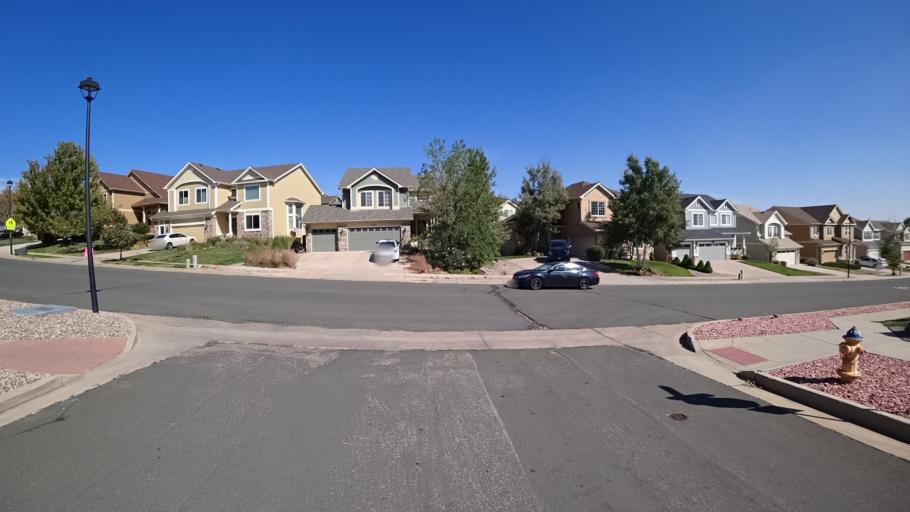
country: US
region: Colorado
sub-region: El Paso County
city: Cimarron Hills
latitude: 38.8944
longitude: -104.6953
